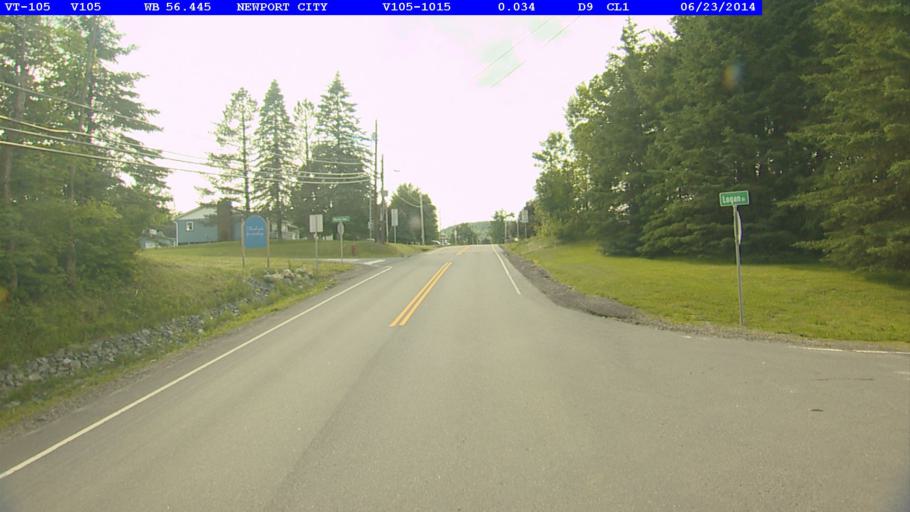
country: US
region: Vermont
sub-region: Orleans County
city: Newport
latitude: 44.9321
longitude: -72.2409
